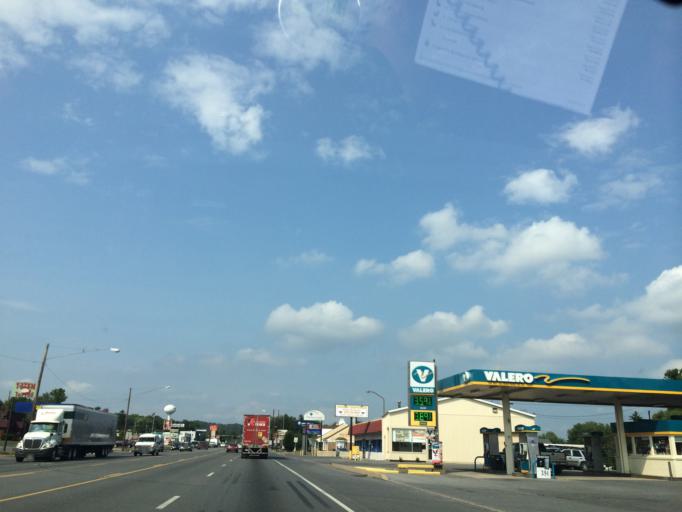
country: US
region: Pennsylvania
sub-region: Snyder County
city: Shamokin Dam
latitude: 40.8459
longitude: -76.8226
